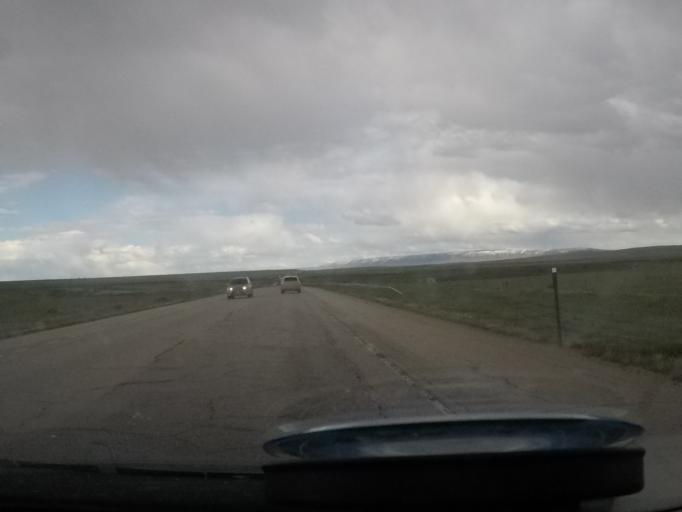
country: US
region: Wyoming
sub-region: Natrona County
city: Mills
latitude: 42.9538
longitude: -106.6426
